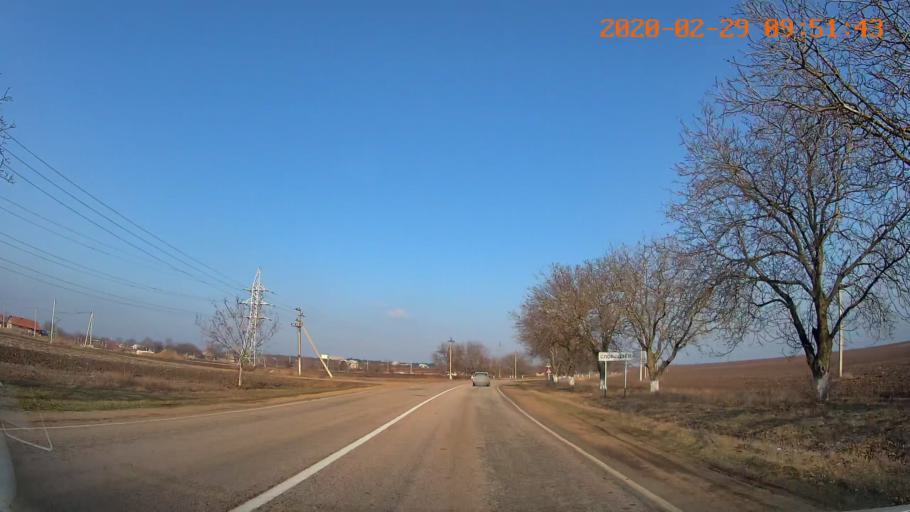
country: MD
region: Telenesti
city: Slobozia
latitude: 46.7107
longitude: 29.7362
